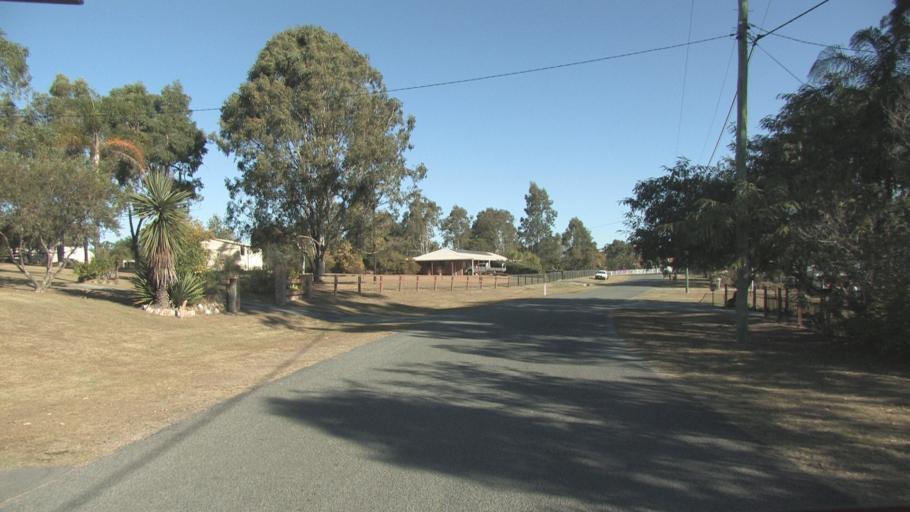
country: AU
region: Queensland
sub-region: Logan
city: North Maclean
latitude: -27.8270
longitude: 153.0210
